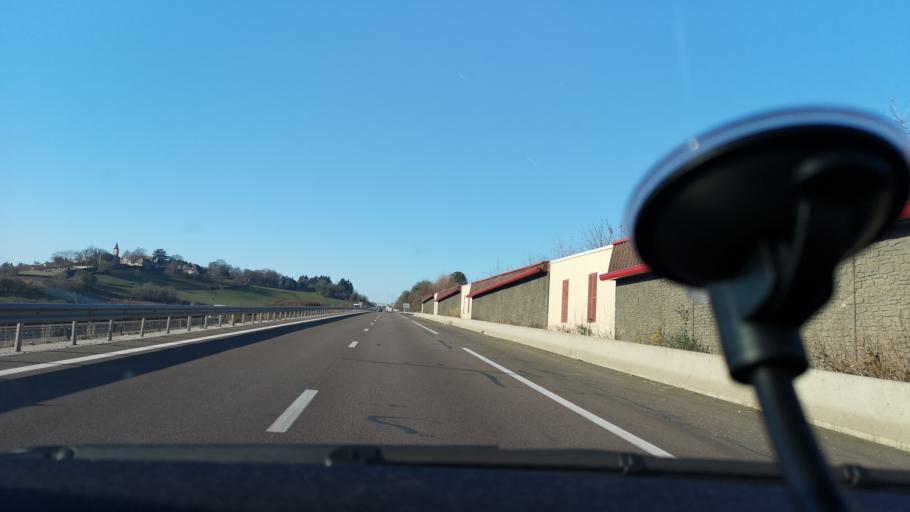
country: FR
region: Bourgogne
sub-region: Departement de Saone-et-Loire
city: Buxy
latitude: 46.7550
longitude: 4.6909
